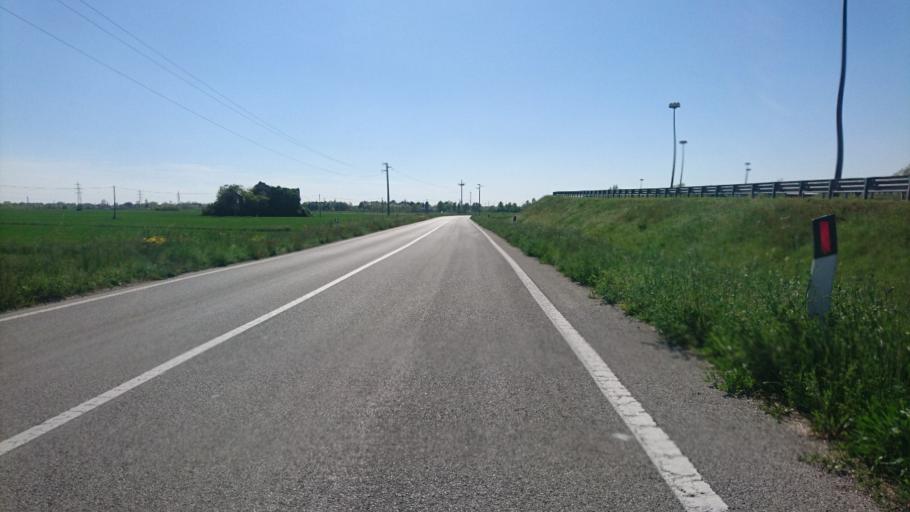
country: IT
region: Veneto
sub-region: Provincia di Venezia
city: Dese
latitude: 45.5333
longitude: 12.2806
